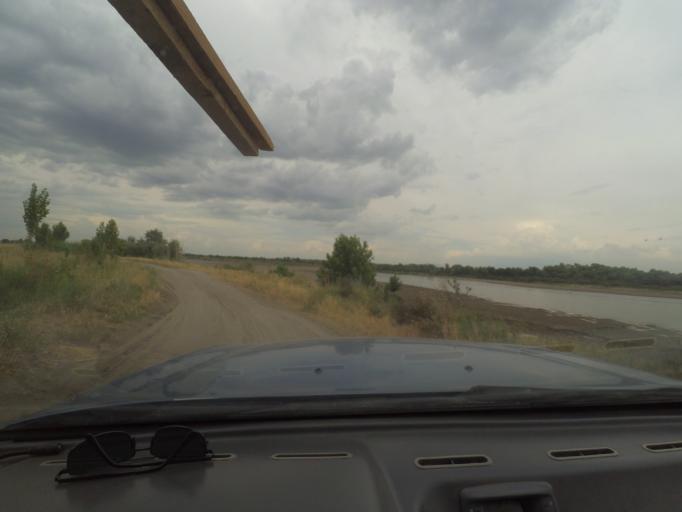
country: TJ
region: Viloyati Sughd
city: Buston
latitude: 40.5406
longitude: 69.0789
